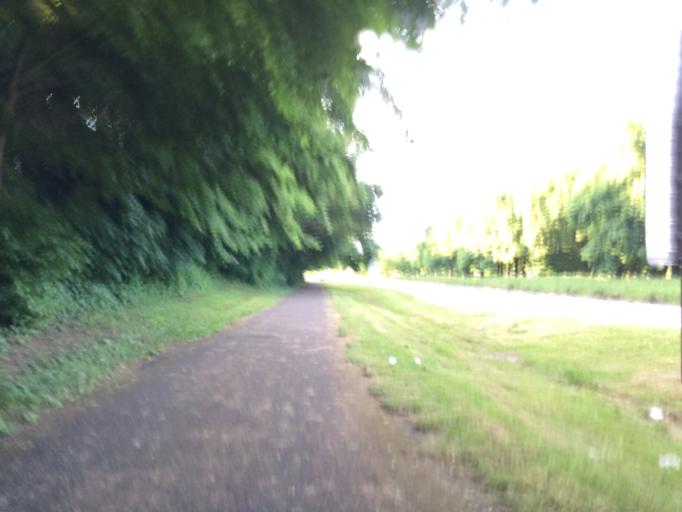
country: FR
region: Ile-de-France
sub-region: Departement de l'Essonne
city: Lisses
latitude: 48.6153
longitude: 2.4224
